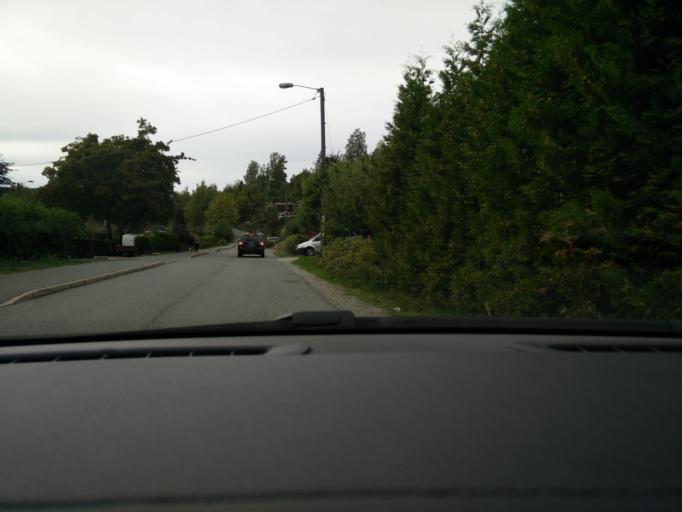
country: NO
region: Akershus
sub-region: Asker
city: Blakstad
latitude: 59.8240
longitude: 10.4653
